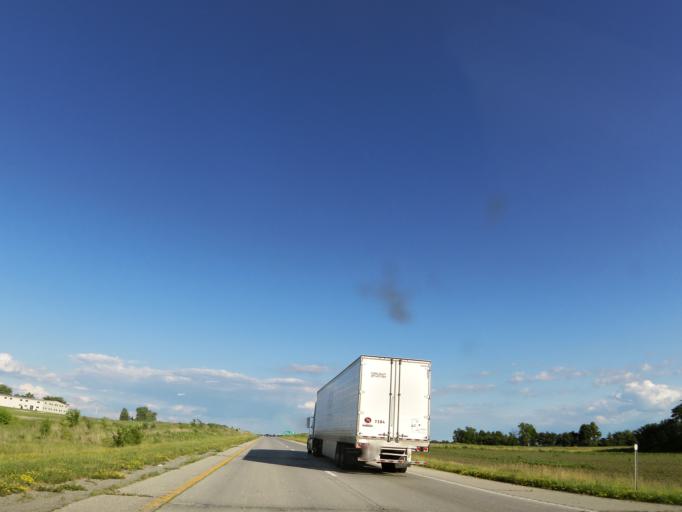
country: US
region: Missouri
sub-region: Pike County
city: Bowling Green
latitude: 39.2732
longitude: -91.0892
